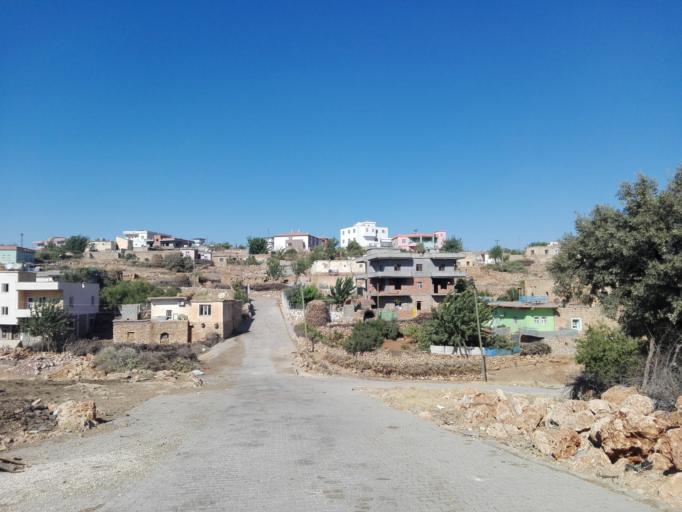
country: TR
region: Mardin
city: Kilavuz
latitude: 37.4804
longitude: 41.7794
